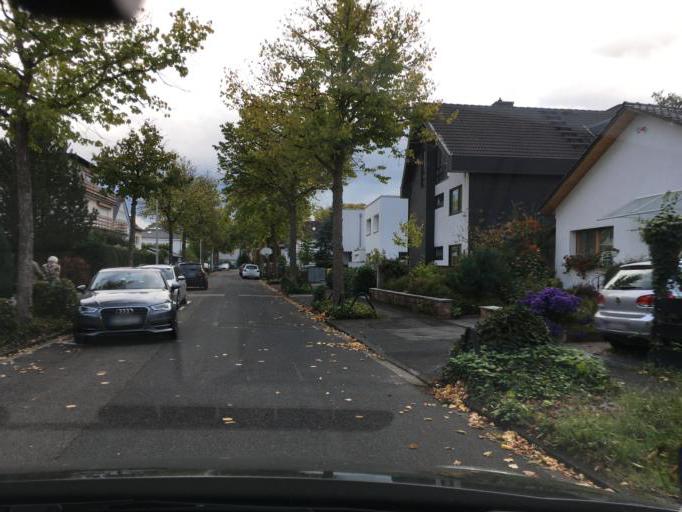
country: DE
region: North Rhine-Westphalia
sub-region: Regierungsbezirk Koln
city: Konigswinter
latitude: 50.6812
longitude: 7.1730
